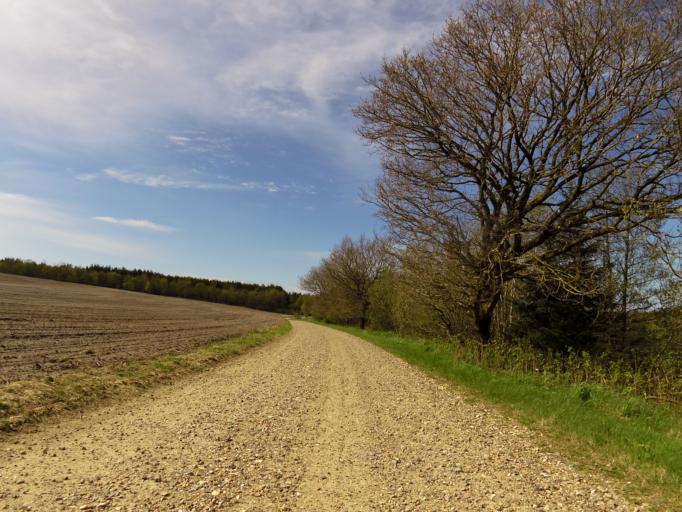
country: DK
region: Central Jutland
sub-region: Holstebro Kommune
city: Vinderup
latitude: 56.4674
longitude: 8.8888
